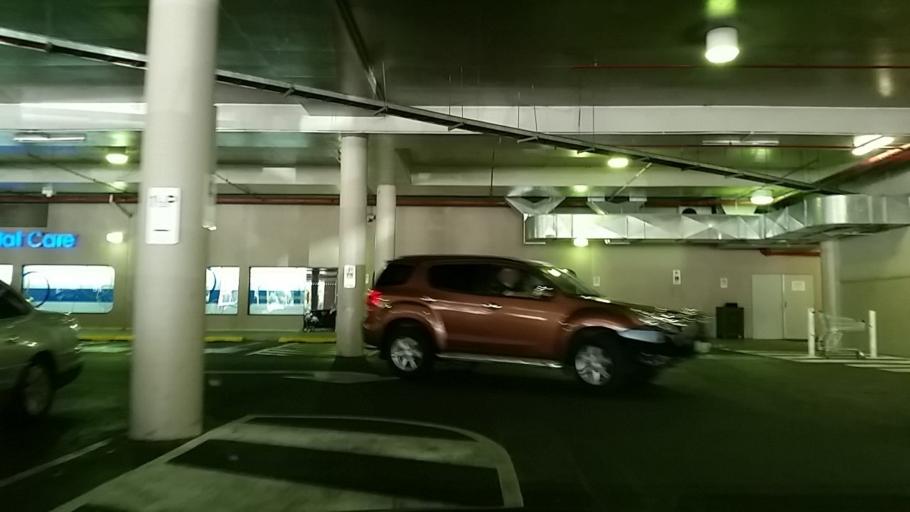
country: AU
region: South Australia
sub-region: Tea Tree Gully
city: Modbury
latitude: -34.8310
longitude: 138.6903
